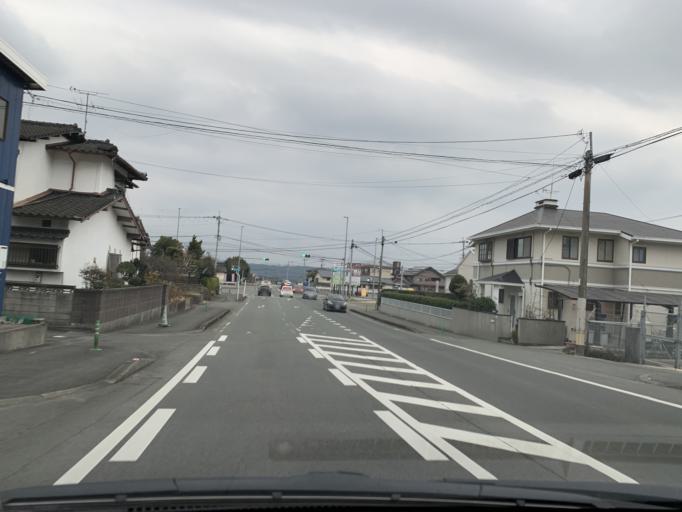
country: JP
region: Kumamoto
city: Ozu
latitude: 32.8809
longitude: 130.8769
